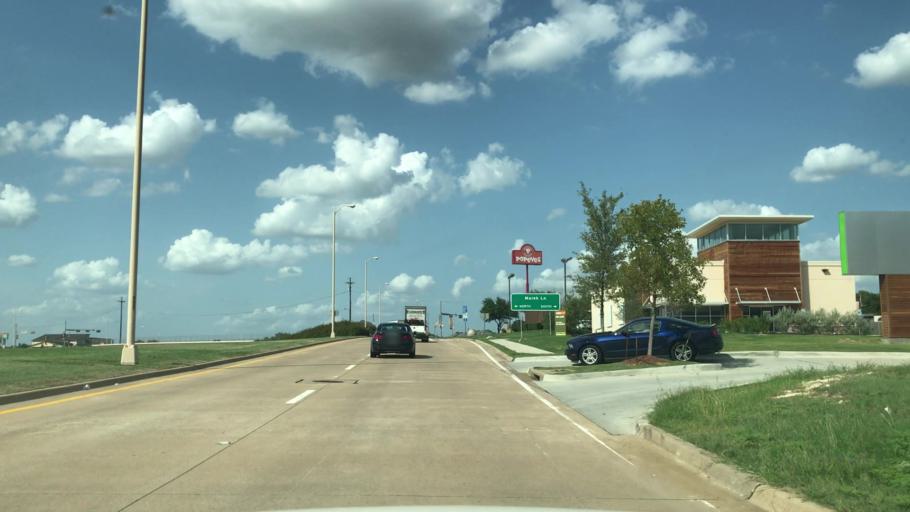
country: US
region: Texas
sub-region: Dallas County
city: Addison
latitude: 32.9988
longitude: -96.8574
